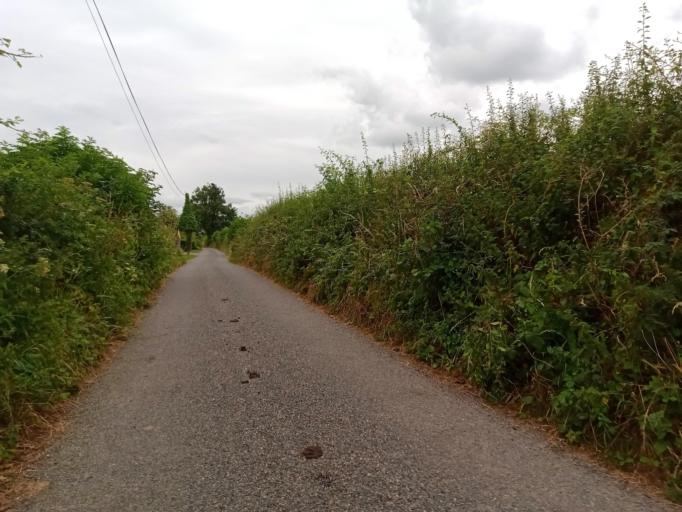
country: IE
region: Leinster
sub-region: Kilkenny
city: Callan
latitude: 52.5439
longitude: -7.4129
